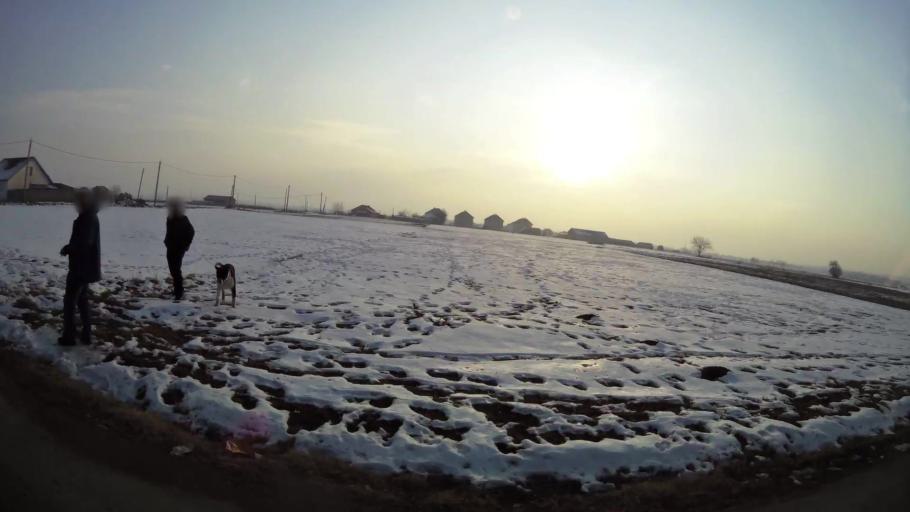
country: MK
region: Aracinovo
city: Arachinovo
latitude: 42.0117
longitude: 21.5293
